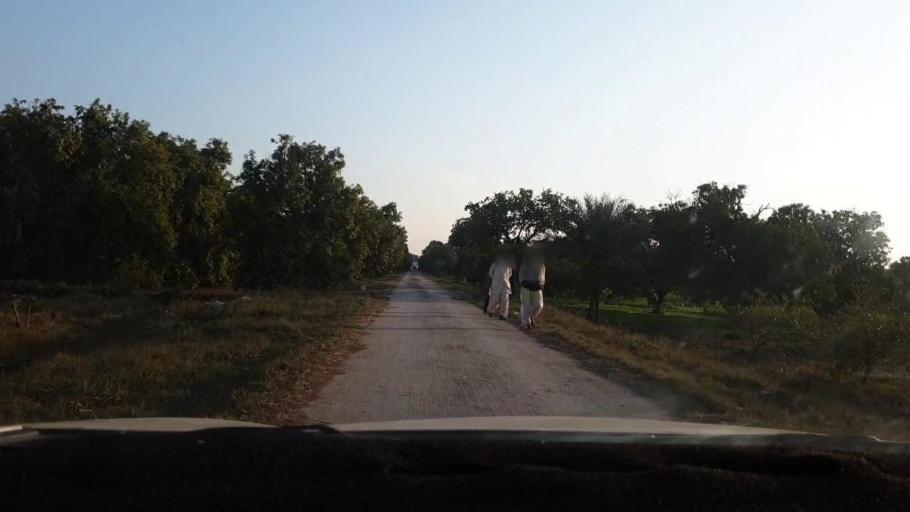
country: PK
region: Sindh
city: Berani
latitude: 25.7783
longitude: 68.7742
